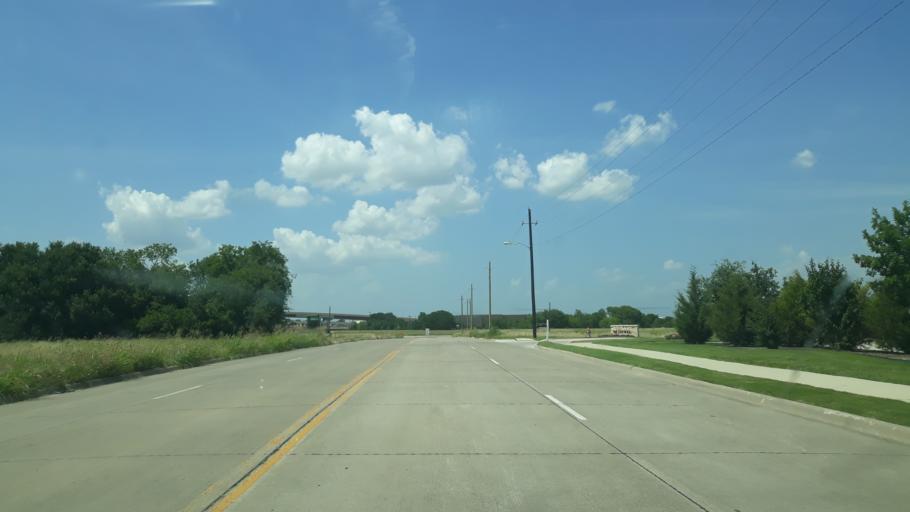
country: US
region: Texas
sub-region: Dallas County
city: Coppell
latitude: 32.9582
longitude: -97.0365
